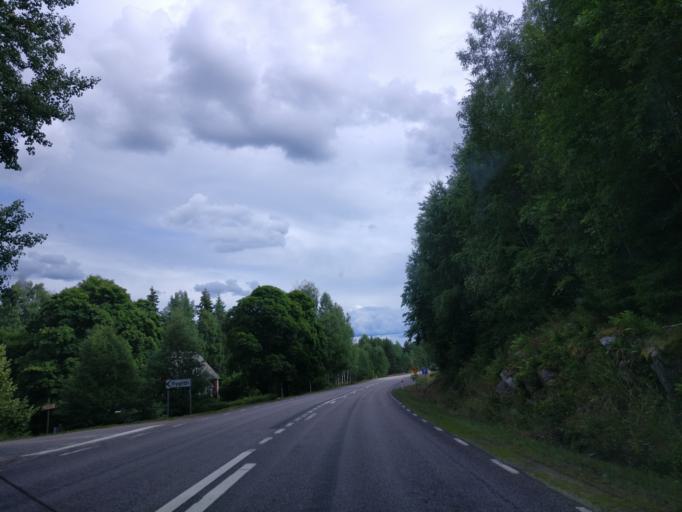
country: SE
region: Vaermland
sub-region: Hagfors Kommun
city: Ekshaerad
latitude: 60.1570
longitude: 13.5147
